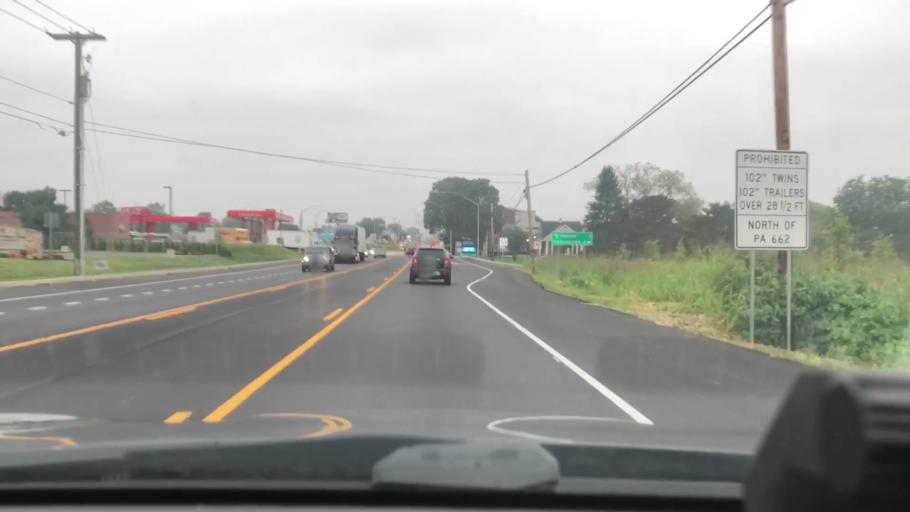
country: US
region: Pennsylvania
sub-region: Berks County
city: Fleetwood
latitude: 40.4866
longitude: -75.8364
